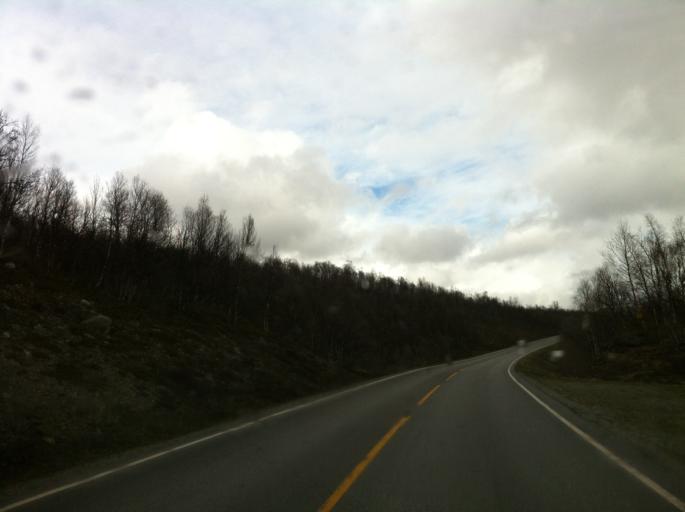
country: NO
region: Sor-Trondelag
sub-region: Tydal
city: Aas
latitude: 62.6375
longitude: 11.9106
